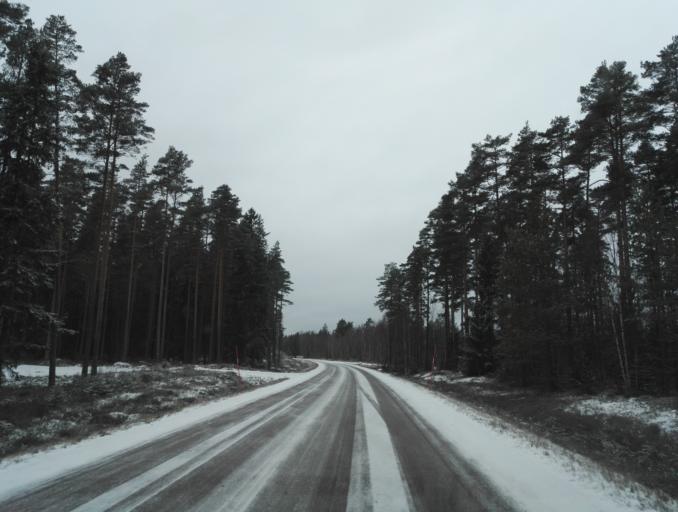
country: SE
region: Kronoberg
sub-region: Lessebo Kommun
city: Lessebo
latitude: 56.7391
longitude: 15.2547
